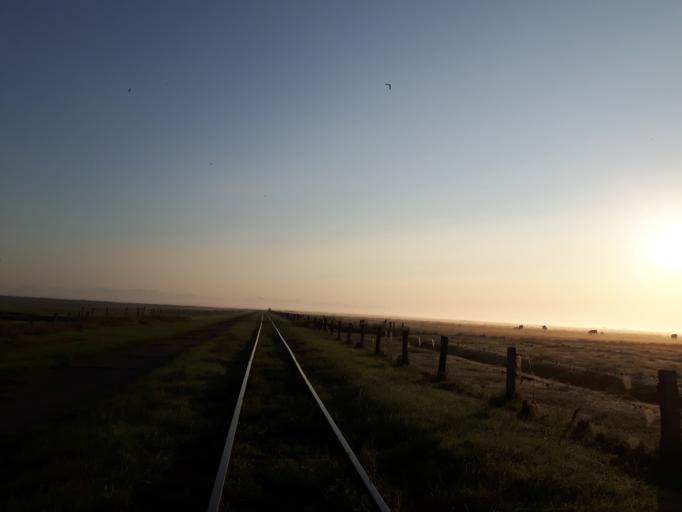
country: DE
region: Schleswig-Holstein
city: Grode
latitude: 54.6770
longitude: 8.7041
